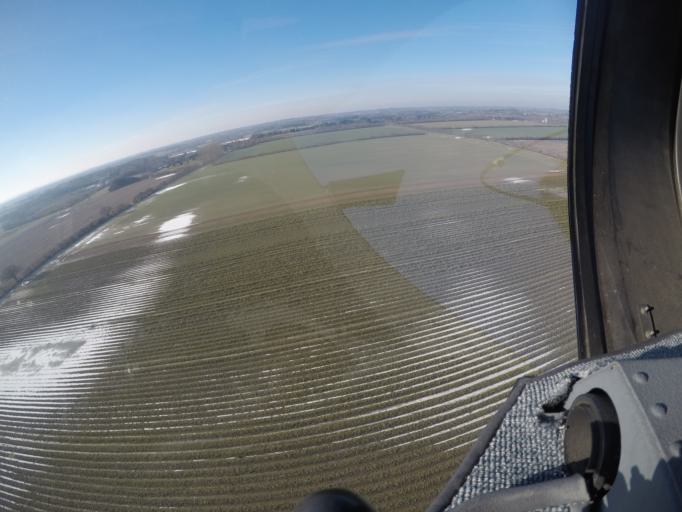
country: DK
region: South Denmark
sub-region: Kolding Kommune
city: Kolding
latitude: 55.5608
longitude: 9.4531
